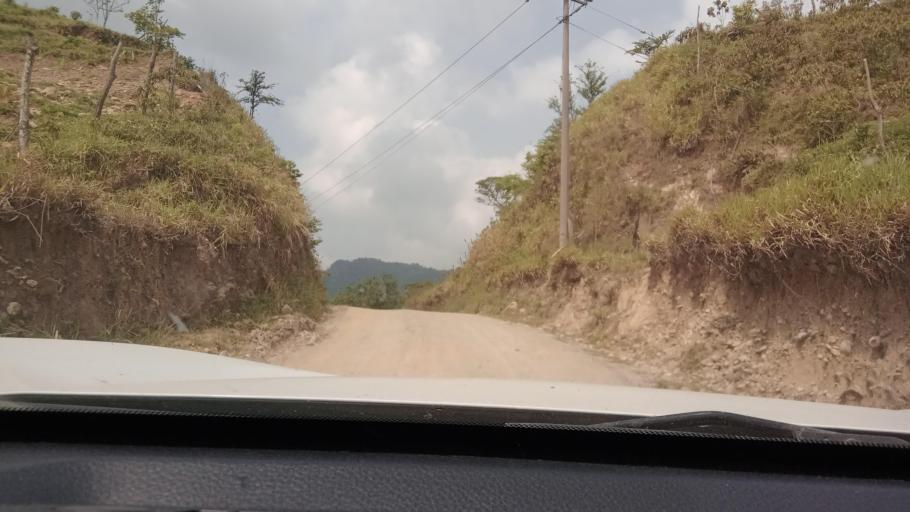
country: MX
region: Tabasco
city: Chontalpa
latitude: 17.4921
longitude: -93.6648
